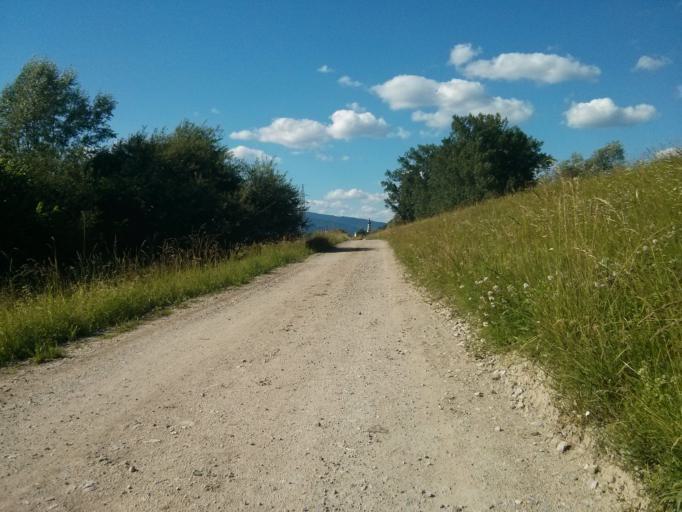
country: DE
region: Bavaria
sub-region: Lower Bavaria
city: Deggendorf
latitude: 48.8144
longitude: 12.9642
